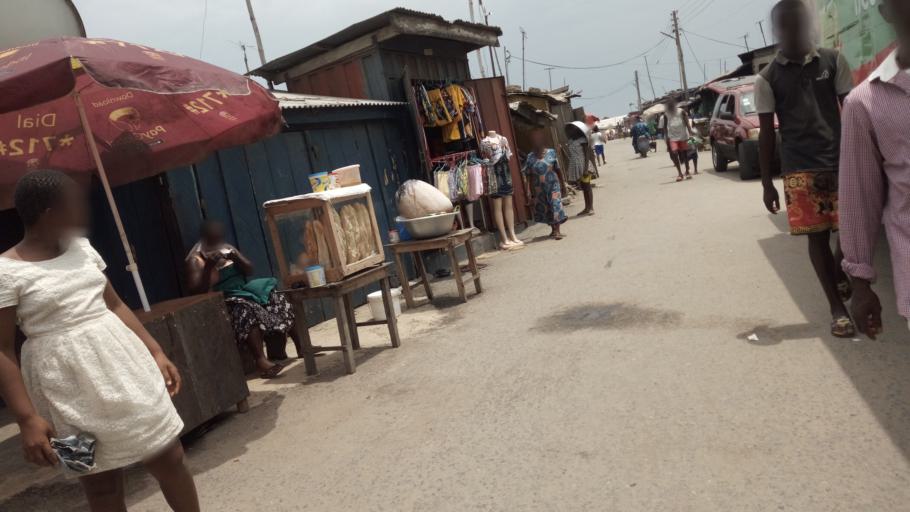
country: GH
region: Central
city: Winneba
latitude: 5.3408
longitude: -0.6186
